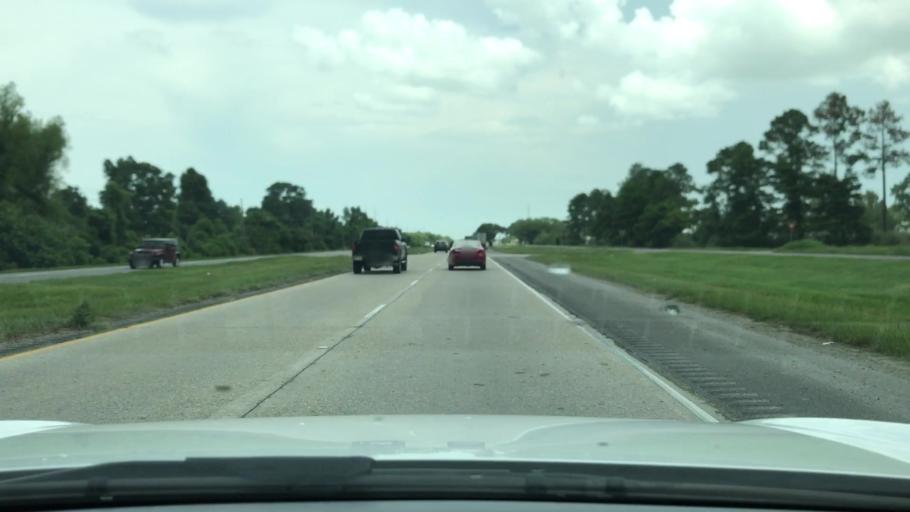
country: US
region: Louisiana
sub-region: Iberville Parish
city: Plaquemine
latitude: 30.3177
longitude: -91.2503
